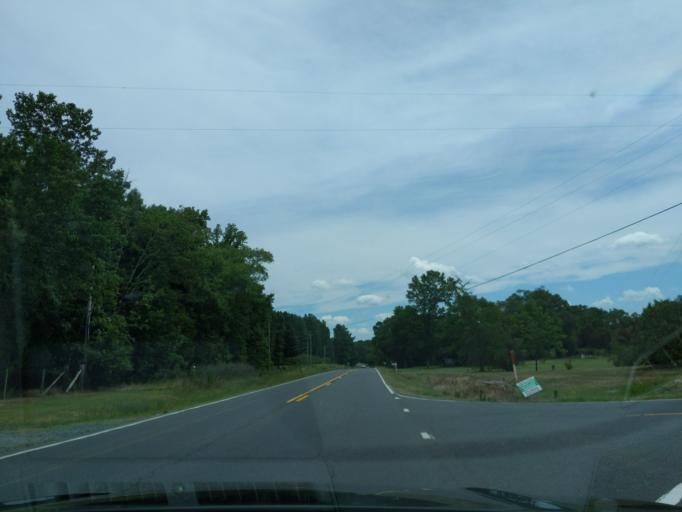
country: US
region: North Carolina
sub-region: Rowan County
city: Rockwell
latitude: 35.4591
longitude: -80.3219
